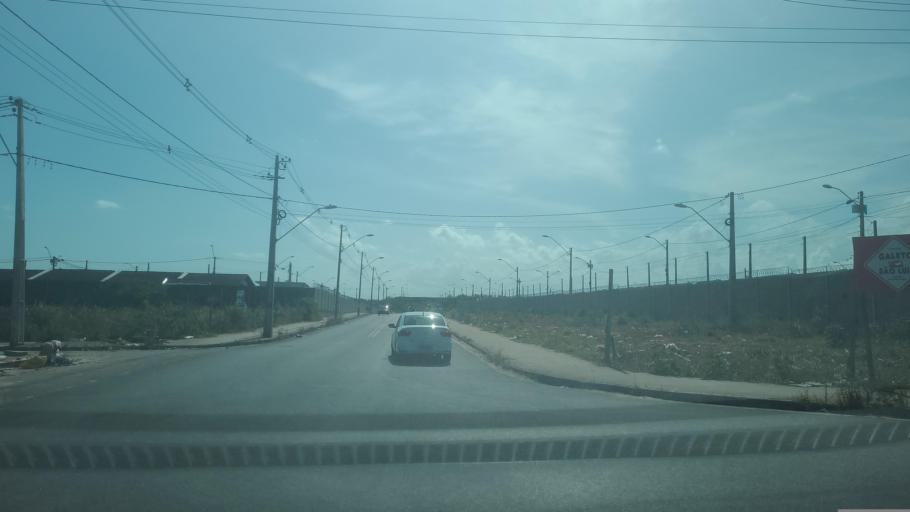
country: BR
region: Alagoas
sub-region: Satuba
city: Satuba
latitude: -9.5260
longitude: -35.7751
